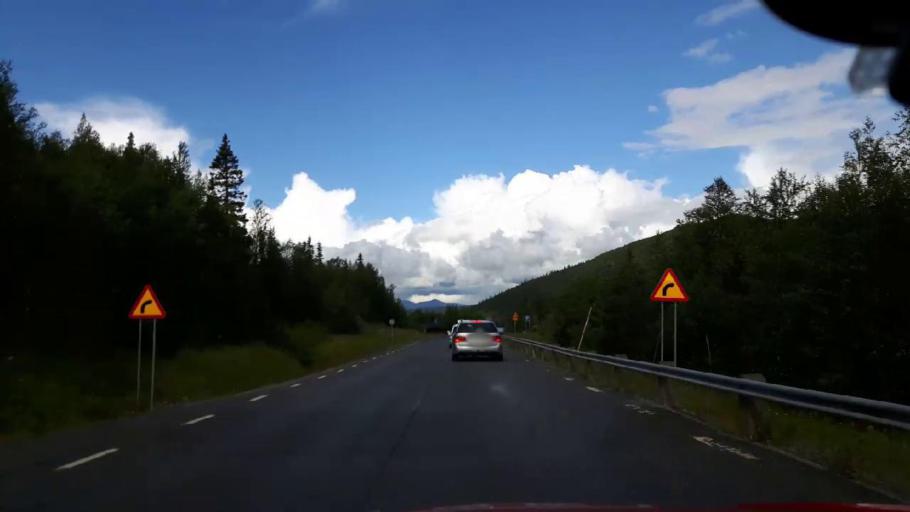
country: SE
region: Vaesterbotten
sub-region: Vilhelmina Kommun
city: Sjoberg
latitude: 65.0293
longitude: 15.1416
